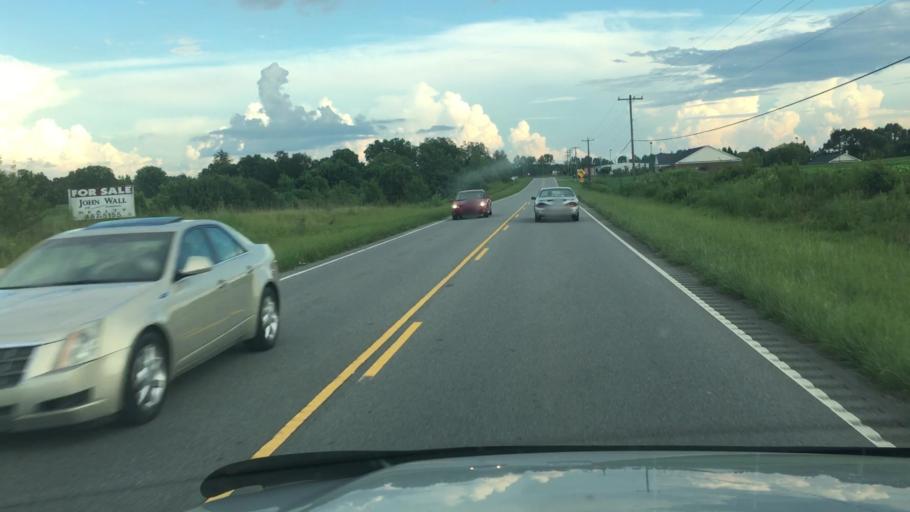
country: US
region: South Carolina
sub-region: Cherokee County
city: Gaffney
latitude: 35.1101
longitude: -81.6993
